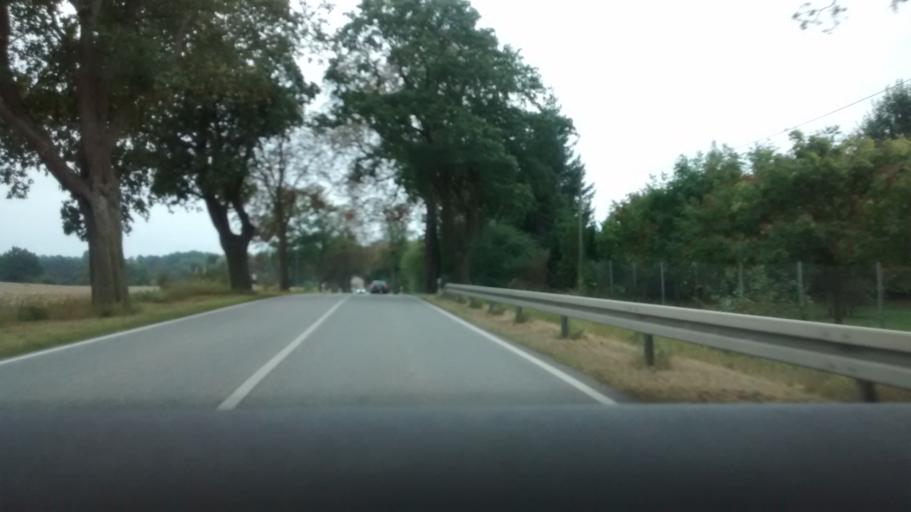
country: DE
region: Mecklenburg-Vorpommern
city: Mecklenburg
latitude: 53.8075
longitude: 11.4351
